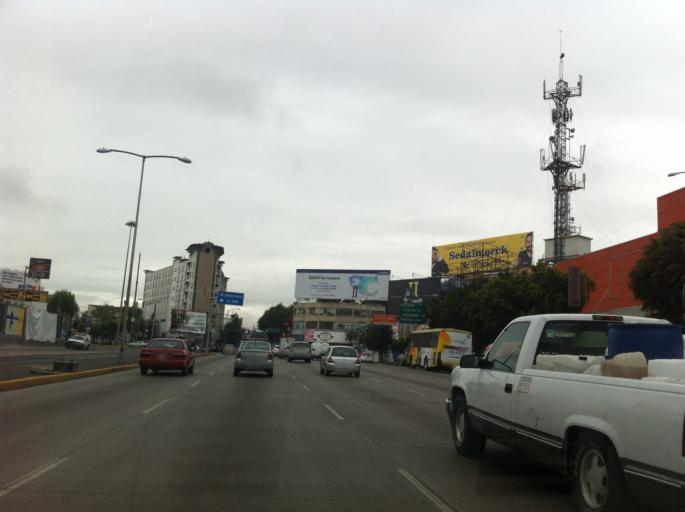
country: MX
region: Mexico City
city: Polanco
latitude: 19.4090
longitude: -99.1837
